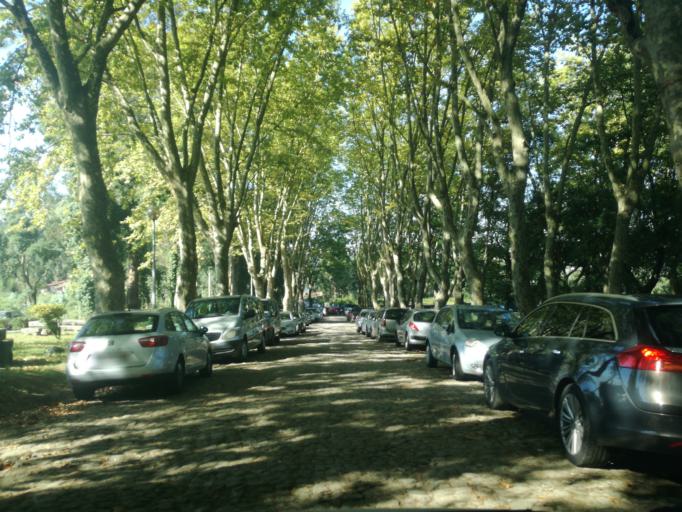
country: PT
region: Porto
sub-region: Maia
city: Leca do Bailio
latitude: 41.2109
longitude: -8.6151
